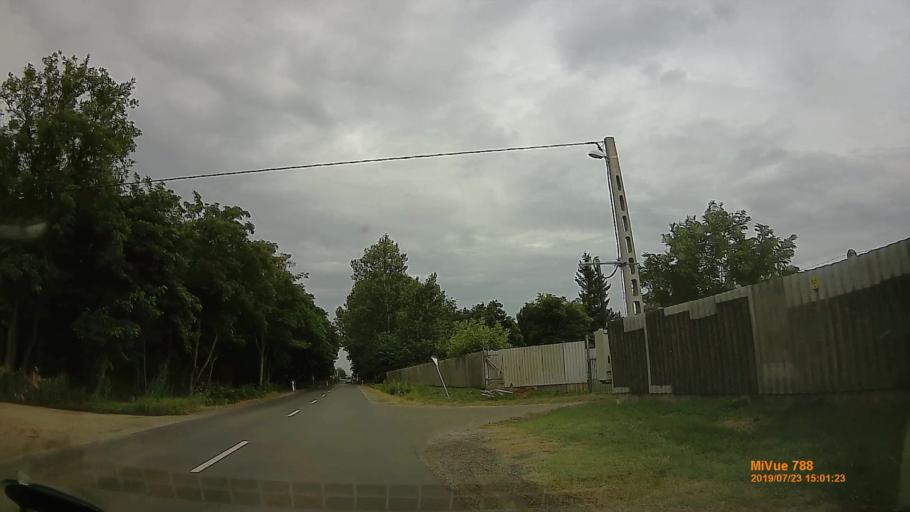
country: HU
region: Szabolcs-Szatmar-Bereg
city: Nyiregyhaza
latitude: 47.9316
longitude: 21.6828
